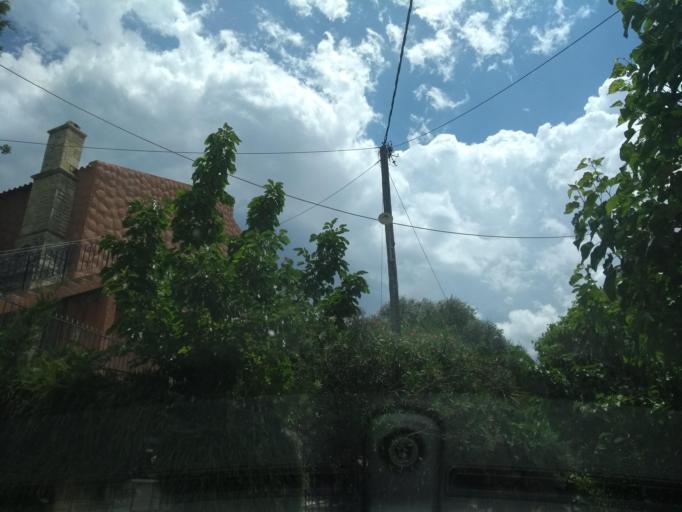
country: GR
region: Crete
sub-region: Nomos Chanias
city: Georgioupolis
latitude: 35.3791
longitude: 24.2462
